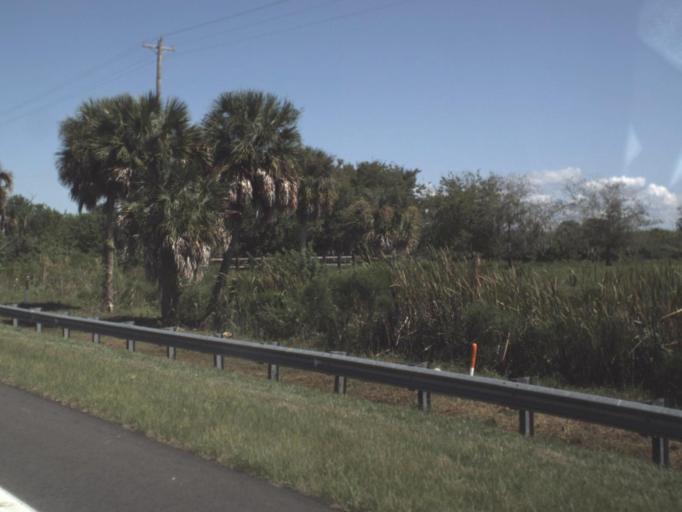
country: US
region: Florida
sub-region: Glades County
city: Buckhead Ridge
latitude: 27.0640
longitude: -80.9790
